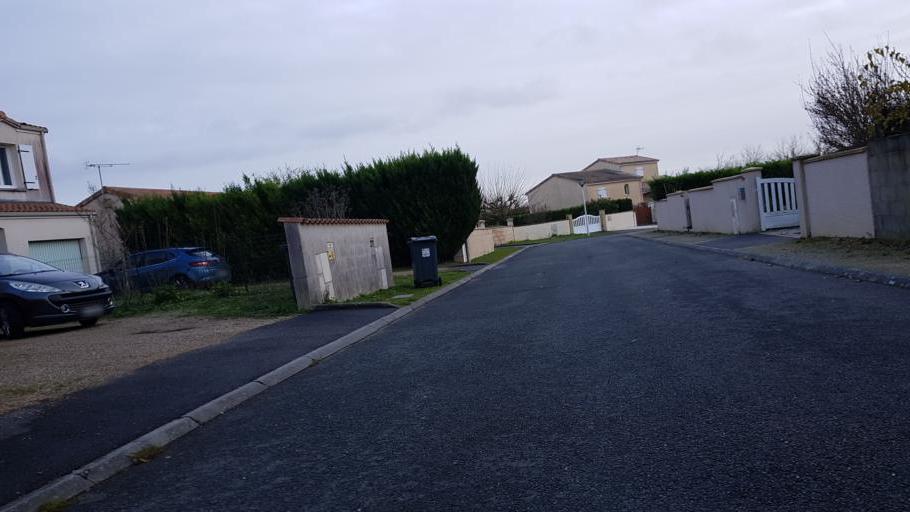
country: FR
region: Poitou-Charentes
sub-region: Departement de la Vienne
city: Avanton
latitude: 46.6612
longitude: 0.3394
